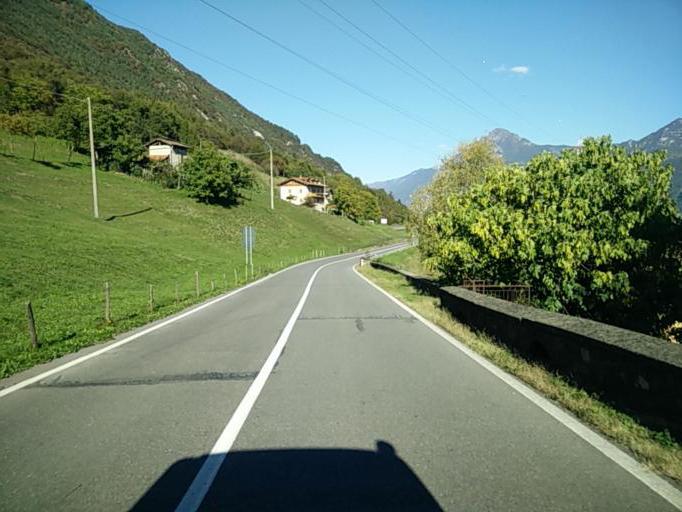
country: IT
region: Lombardy
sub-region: Provincia di Brescia
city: Ponte Caffaro
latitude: 45.8106
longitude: 10.5127
